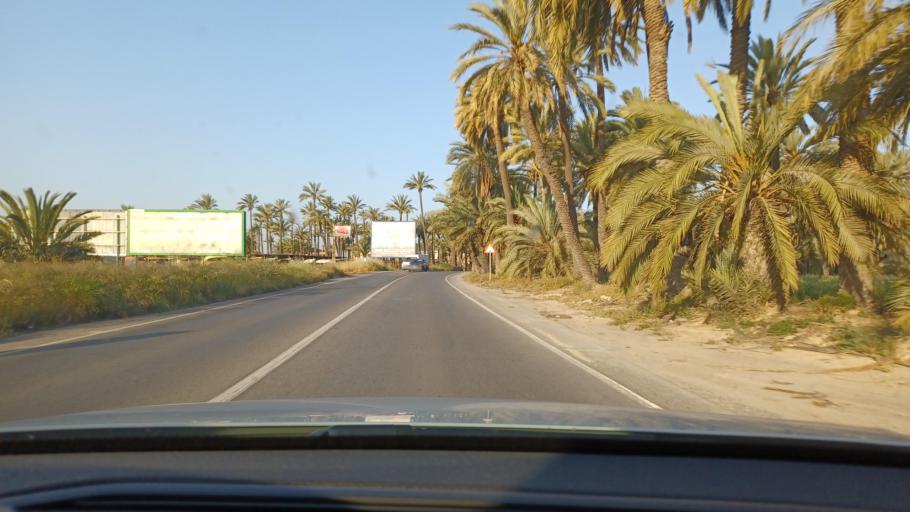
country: ES
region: Valencia
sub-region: Provincia de Alicante
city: Elche
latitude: 38.2577
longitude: -0.6849
